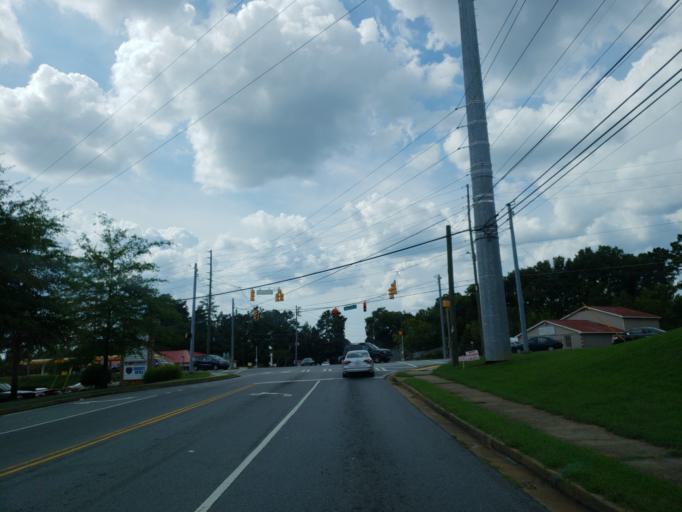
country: US
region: Georgia
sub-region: Cobb County
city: Kennesaw
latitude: 34.0648
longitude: -84.6243
